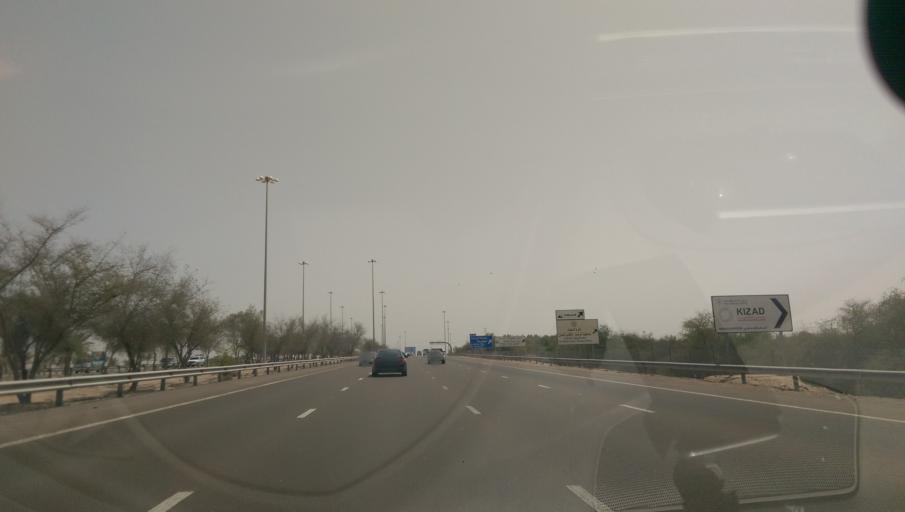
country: AE
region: Abu Dhabi
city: Abu Dhabi
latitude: 24.6466
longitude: 54.7405
